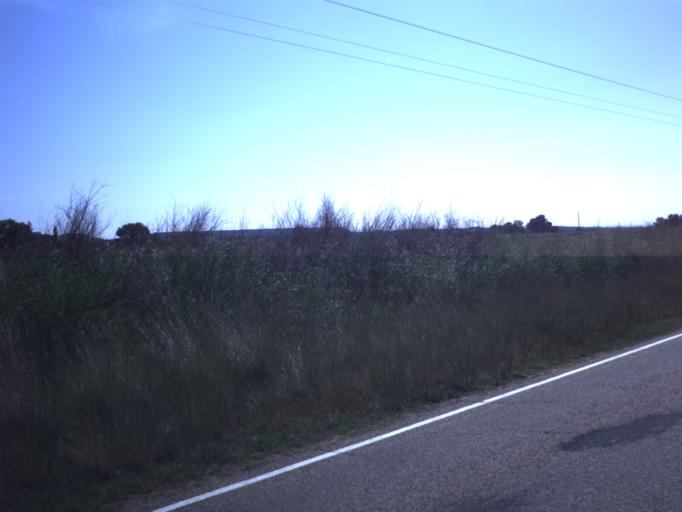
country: US
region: Utah
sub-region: Duchesne County
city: Duchesne
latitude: 40.3174
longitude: -110.2551
